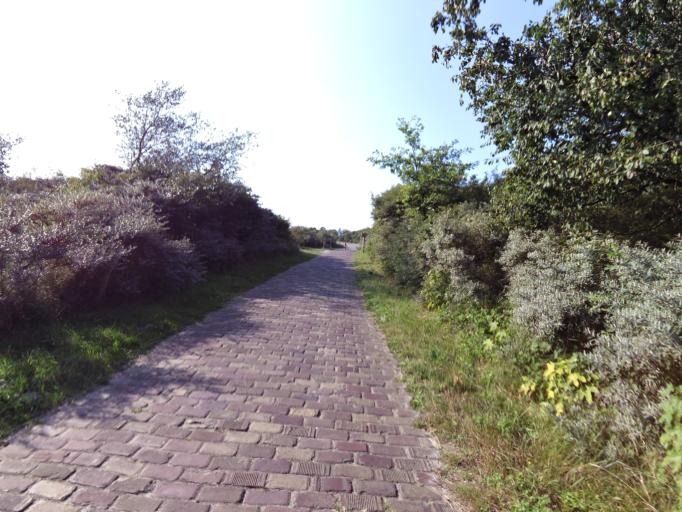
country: NL
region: South Holland
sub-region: Gemeente Rotterdam
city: Hoek van Holland
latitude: 51.9154
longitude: 4.0648
